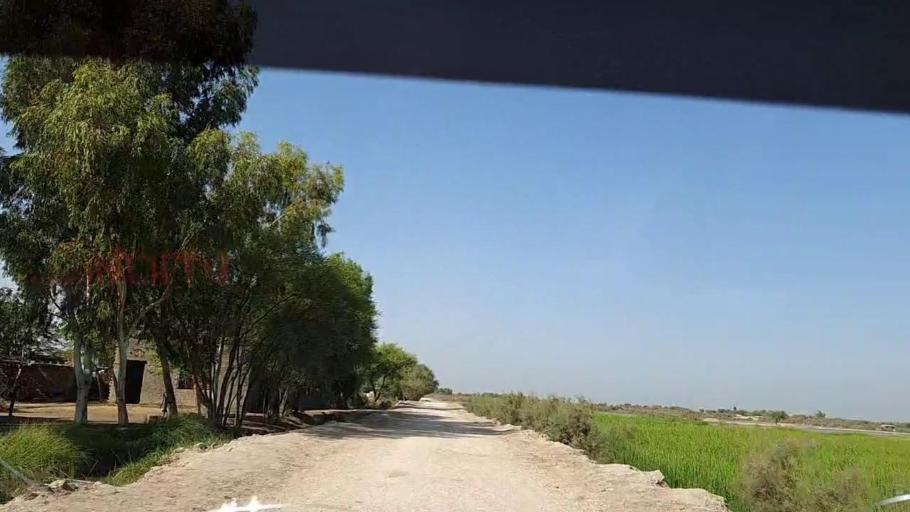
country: PK
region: Sindh
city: Tangwani
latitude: 28.3333
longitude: 69.0725
